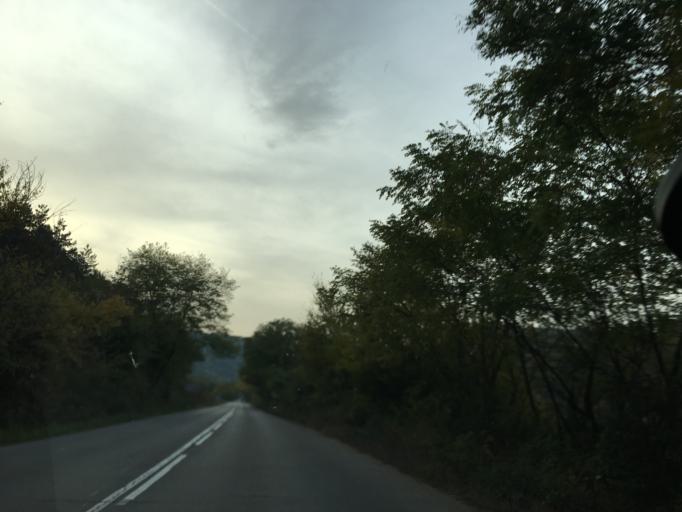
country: BG
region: Pazardzhik
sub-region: Obshtina Belovo
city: Belovo
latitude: 42.2301
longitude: 23.9646
